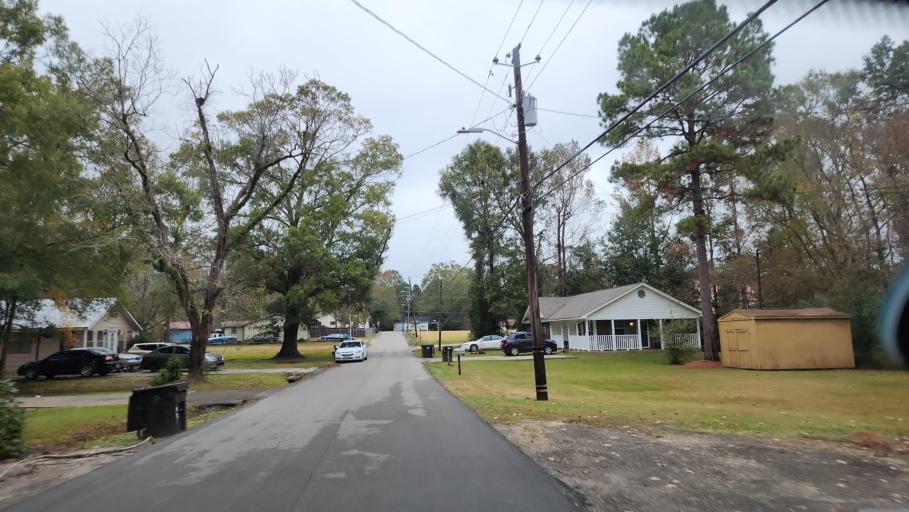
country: US
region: Mississippi
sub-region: Forrest County
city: Hattiesburg
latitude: 31.3012
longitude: -89.3013
